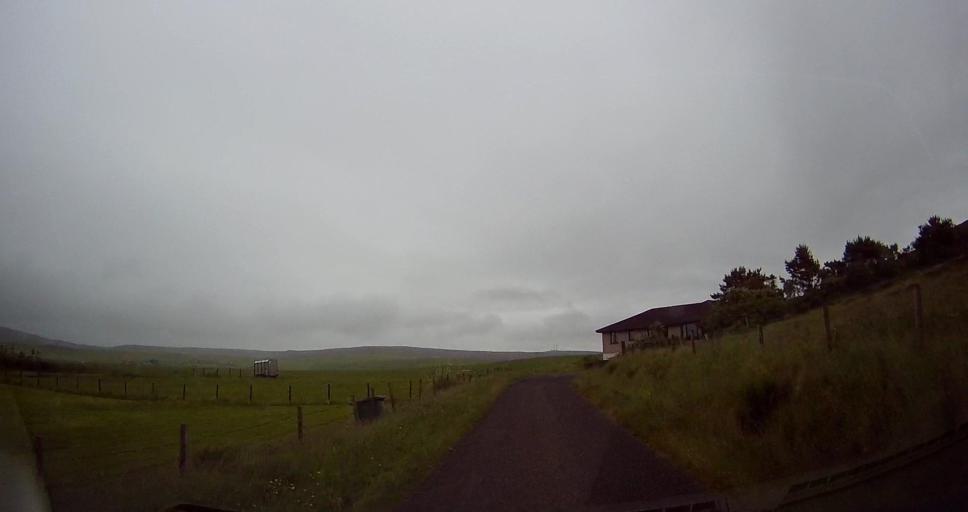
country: GB
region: Scotland
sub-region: Orkney Islands
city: Stromness
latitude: 58.9764
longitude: -3.1584
